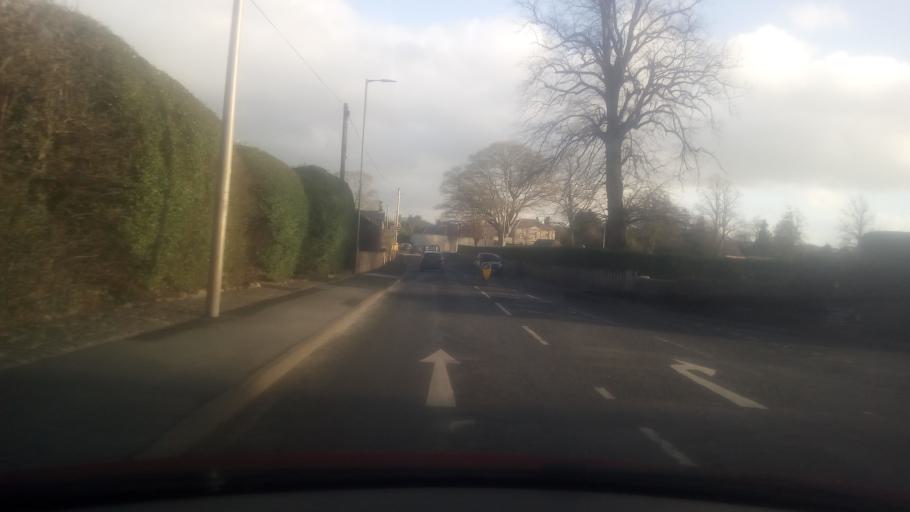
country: GB
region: Scotland
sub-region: The Scottish Borders
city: Kelso
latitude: 55.6018
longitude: -2.4275
